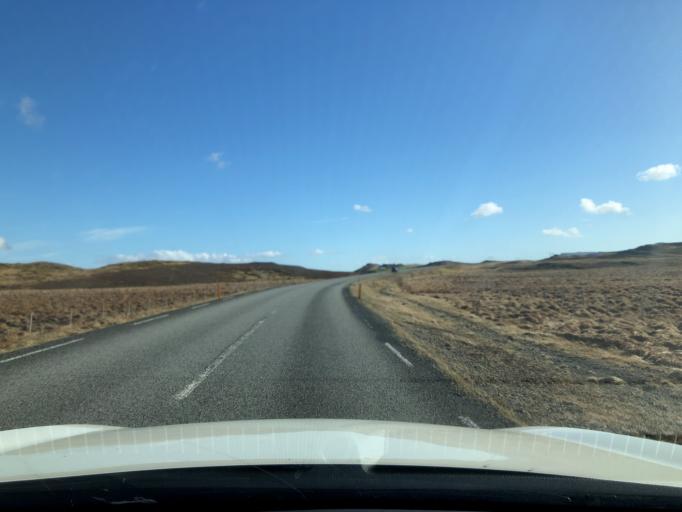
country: IS
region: West
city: Borgarnes
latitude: 64.5577
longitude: -21.7295
